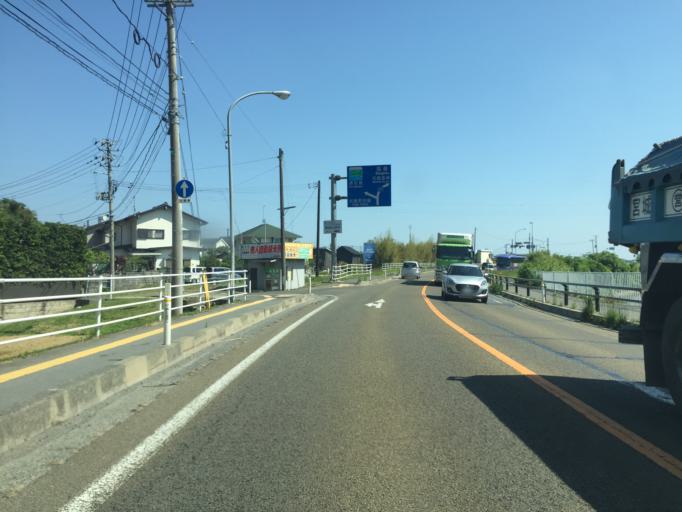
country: JP
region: Miyagi
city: Matsushima
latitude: 38.3922
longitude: 141.0678
